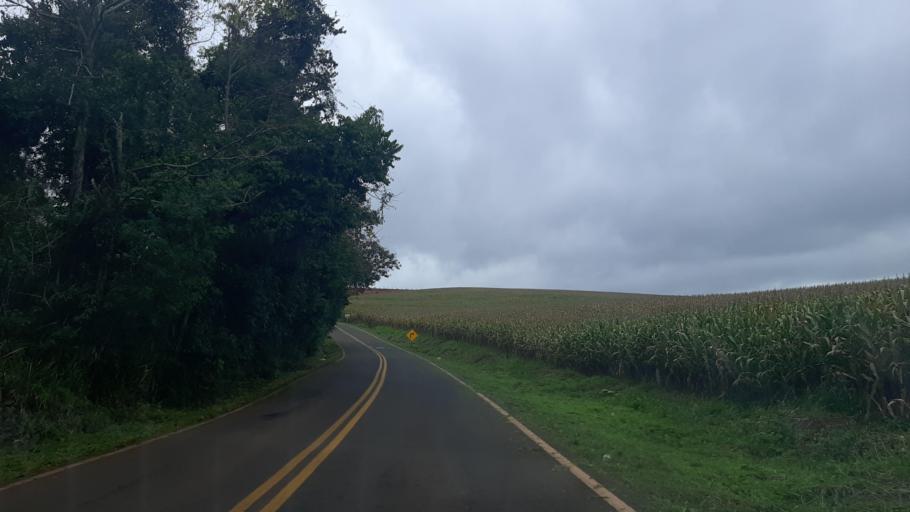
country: BR
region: Parana
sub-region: Ampere
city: Ampere
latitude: -25.9460
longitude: -53.4598
